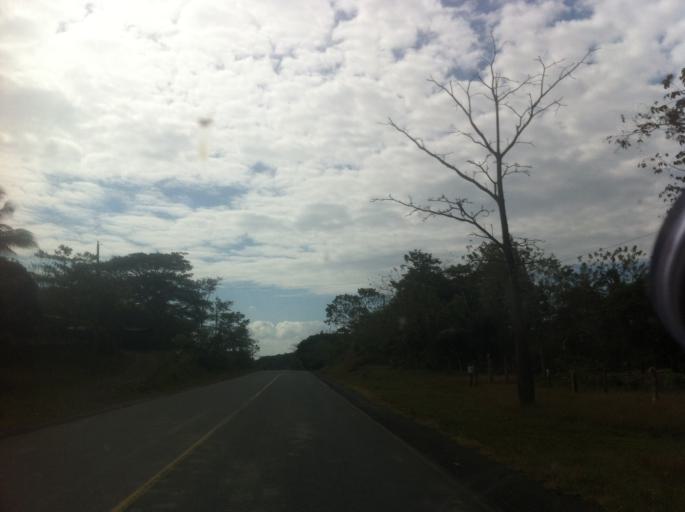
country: NI
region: Rio San Juan
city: San Miguelito
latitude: 11.3337
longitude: -84.7497
